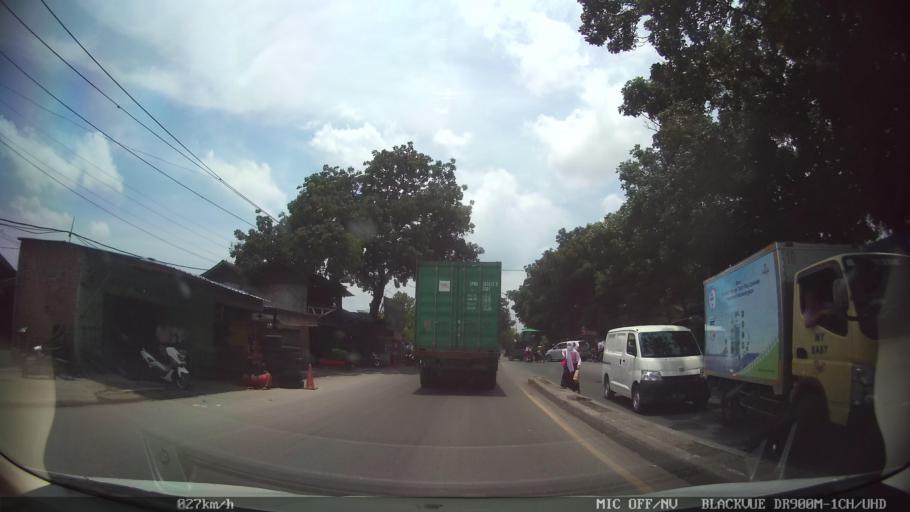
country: ID
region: North Sumatra
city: Labuhan Deli
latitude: 3.7081
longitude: 98.6799
